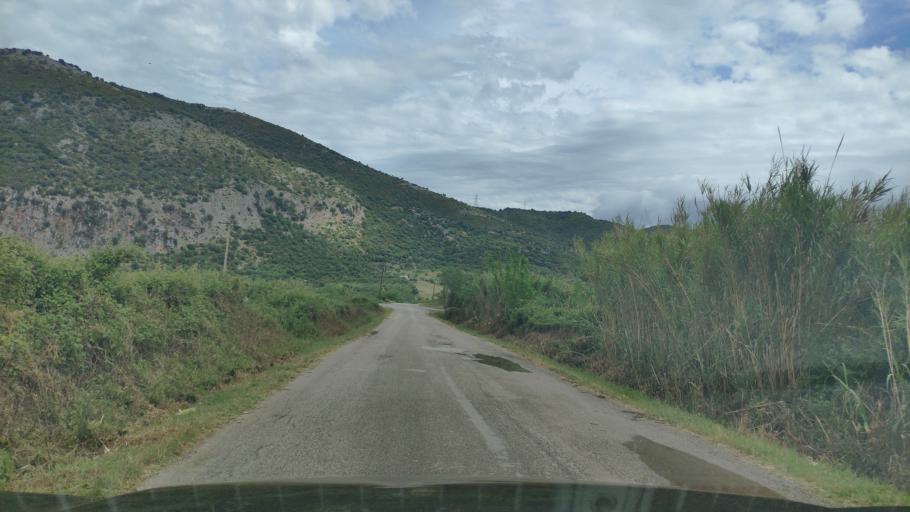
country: GR
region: West Greece
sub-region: Nomos Aitolias kai Akarnanias
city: Vonitsa
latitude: 38.9105
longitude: 20.9058
